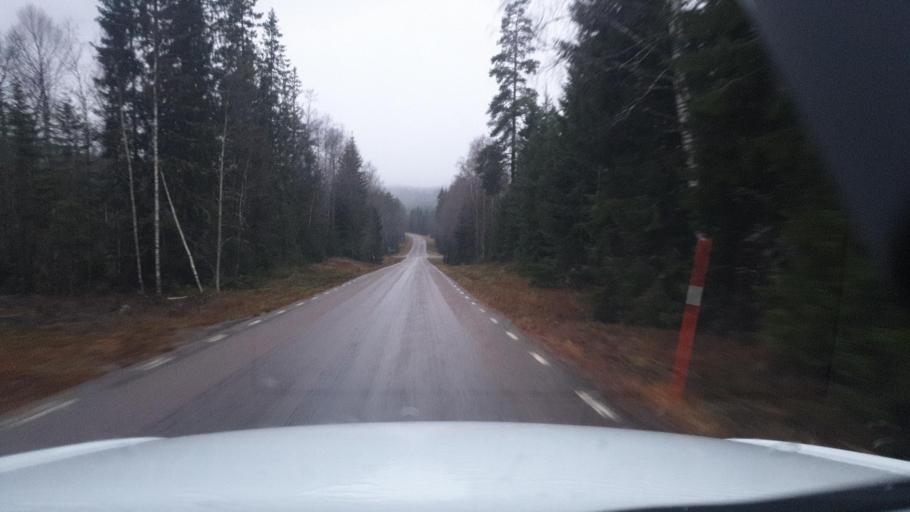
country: SE
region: Vaermland
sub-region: Sunne Kommun
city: Sunne
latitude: 59.8249
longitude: 12.8461
